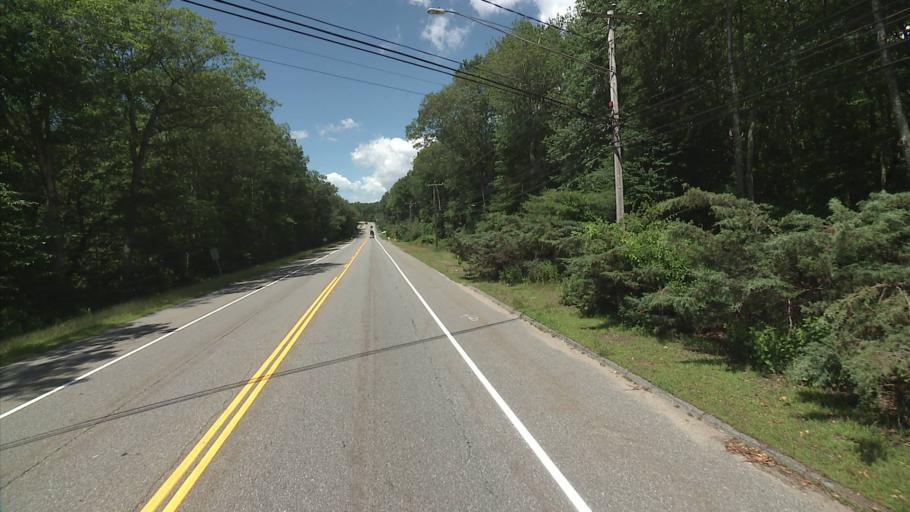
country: US
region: Connecticut
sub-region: New London County
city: Old Mystic
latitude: 41.3897
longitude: -71.9954
